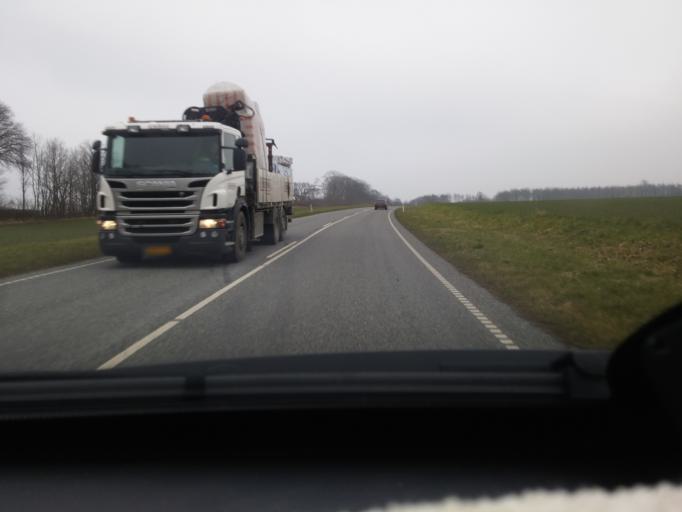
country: DK
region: South Denmark
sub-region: Kerteminde Kommune
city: Kerteminde
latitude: 55.4401
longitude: 10.6804
